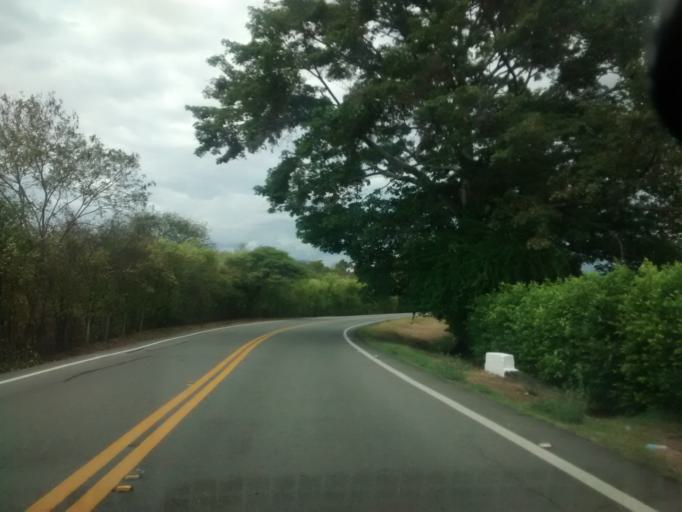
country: CO
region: Cundinamarca
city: Agua de Dios
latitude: 4.4077
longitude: -74.7189
